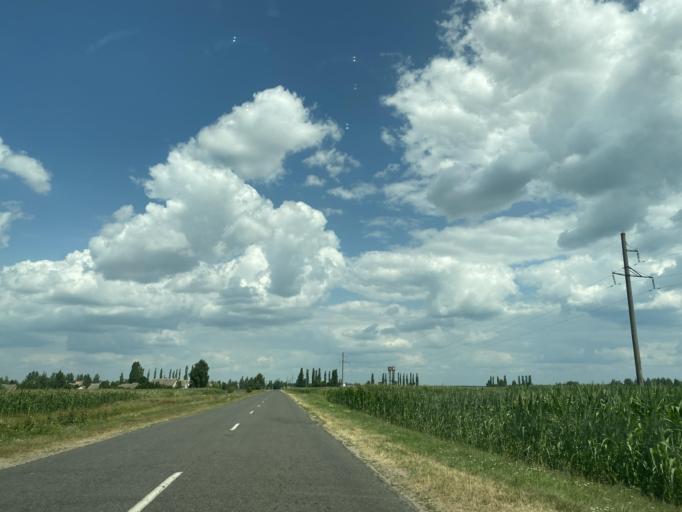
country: BY
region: Brest
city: Ivanava
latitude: 52.3408
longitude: 25.6250
